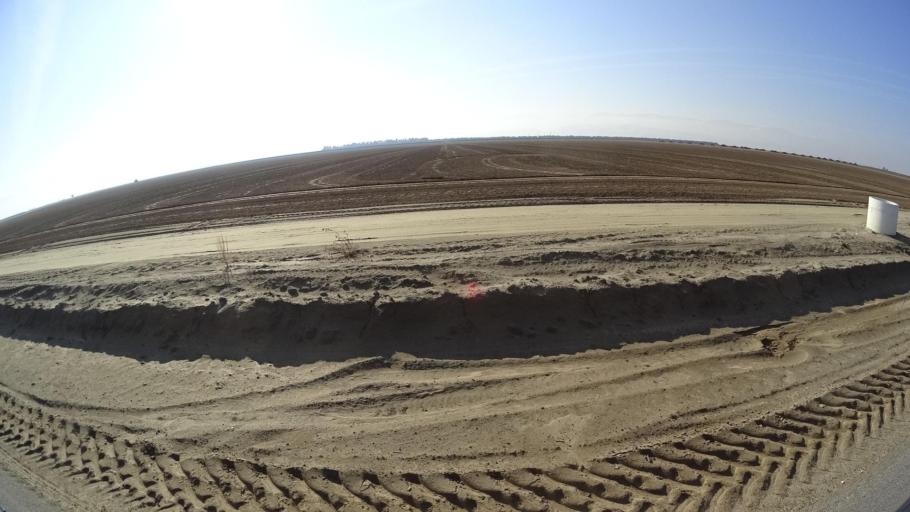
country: US
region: California
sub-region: Kern County
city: Weedpatch
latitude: 35.1221
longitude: -118.9552
